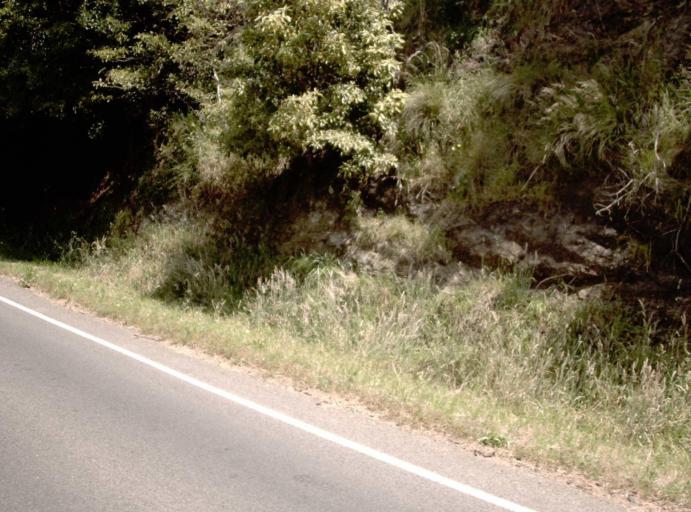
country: AU
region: Victoria
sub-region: Latrobe
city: Traralgon
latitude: -38.3723
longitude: 146.7551
